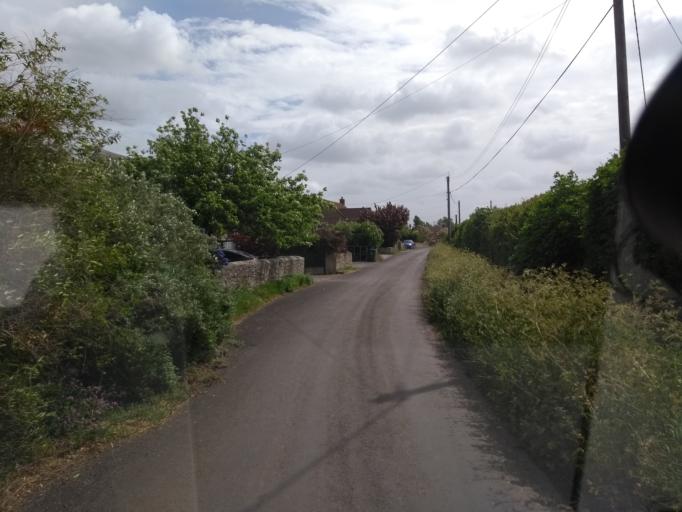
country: GB
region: England
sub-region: Somerset
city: Bridgwater
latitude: 51.1873
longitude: -3.0831
